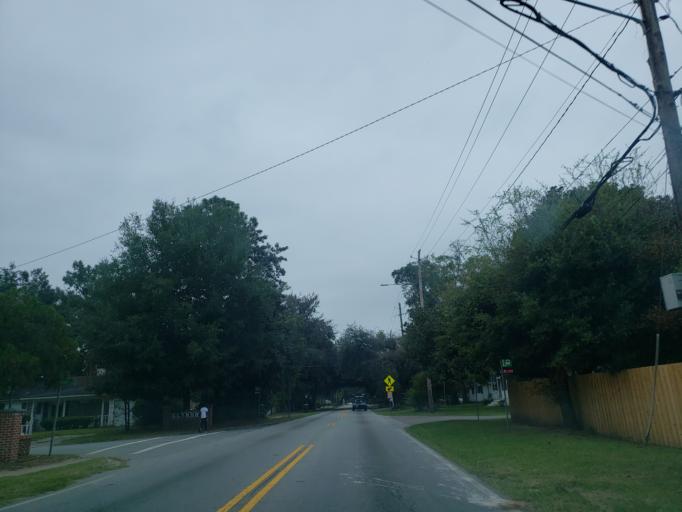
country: US
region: Georgia
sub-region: Chatham County
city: Thunderbolt
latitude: 32.0236
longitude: -81.0729
